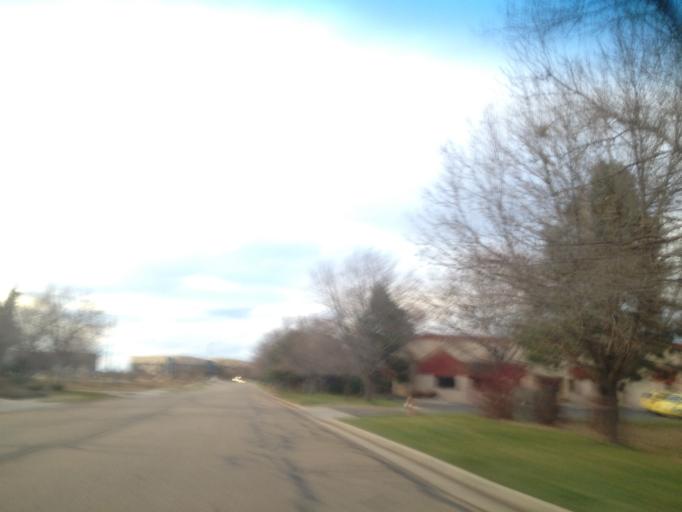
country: US
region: Colorado
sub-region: Boulder County
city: Louisville
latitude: 39.9670
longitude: -105.1196
